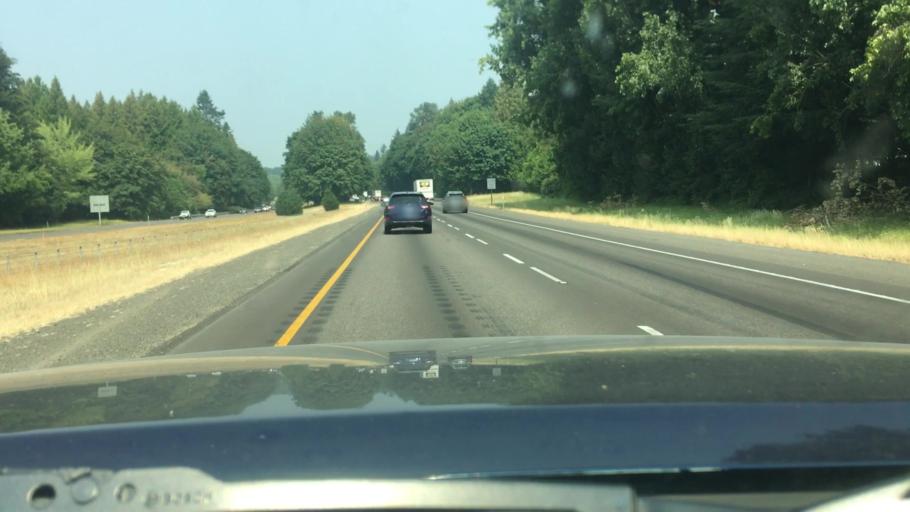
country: US
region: Oregon
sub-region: Clackamas County
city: West Linn
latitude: 45.3550
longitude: -122.6633
